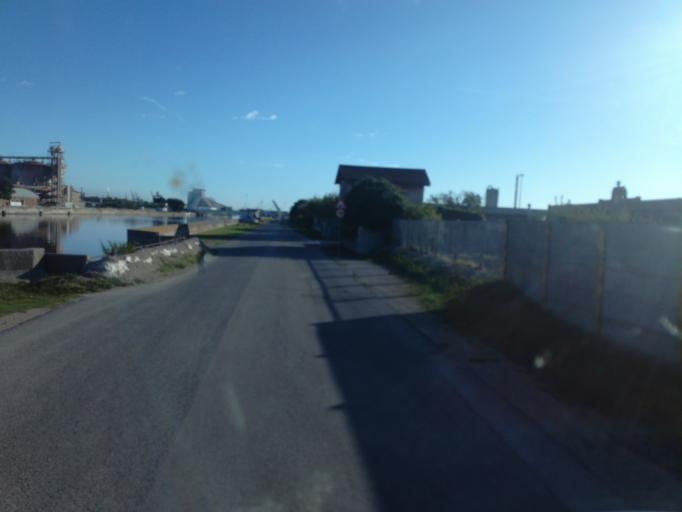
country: IT
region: Emilia-Romagna
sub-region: Provincia di Ravenna
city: Ravenna
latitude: 44.4259
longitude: 12.2207
